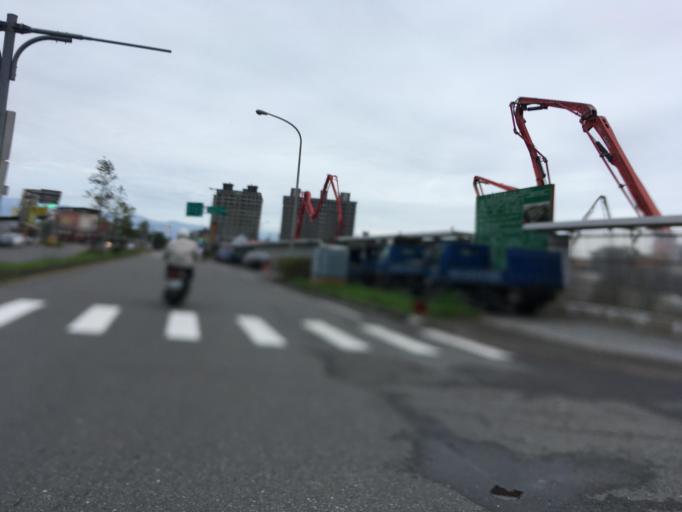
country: TW
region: Taiwan
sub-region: Yilan
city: Yilan
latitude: 24.6860
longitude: 121.7710
